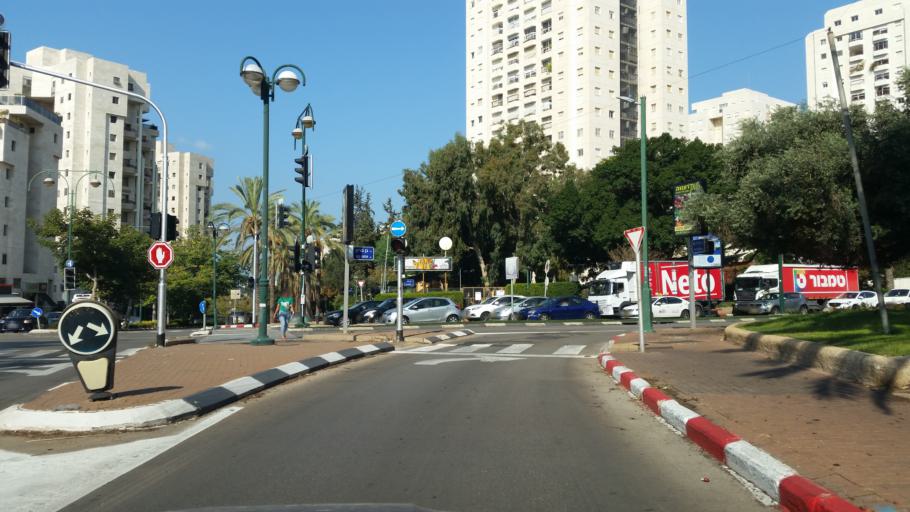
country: IL
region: Tel Aviv
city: Ramat HaSharon
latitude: 32.1516
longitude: 34.8424
